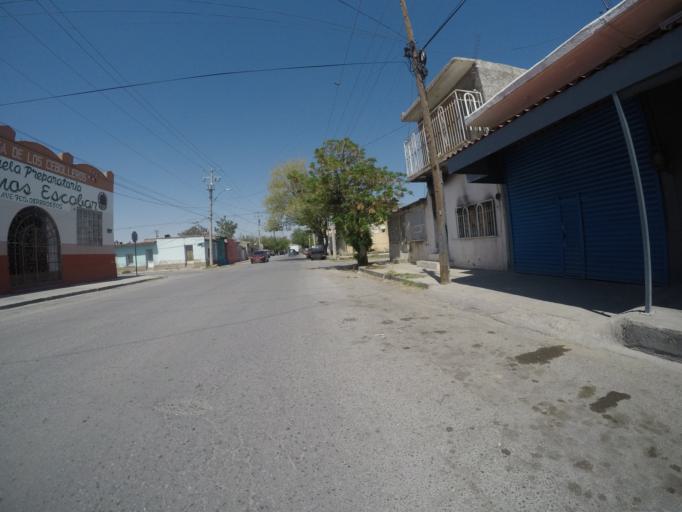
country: MX
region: Chihuahua
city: Ciudad Juarez
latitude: 31.7256
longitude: -106.4797
